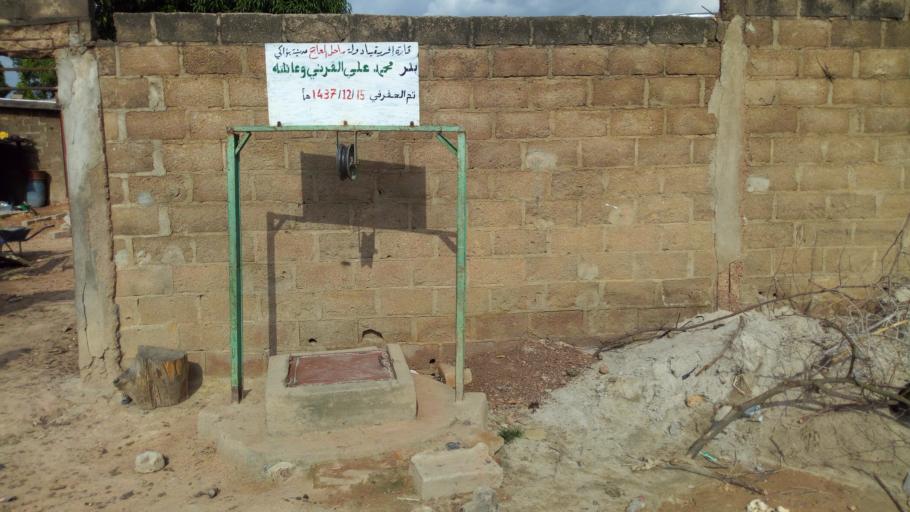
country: CI
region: Vallee du Bandama
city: Bouake
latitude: 7.7294
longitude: -5.0155
